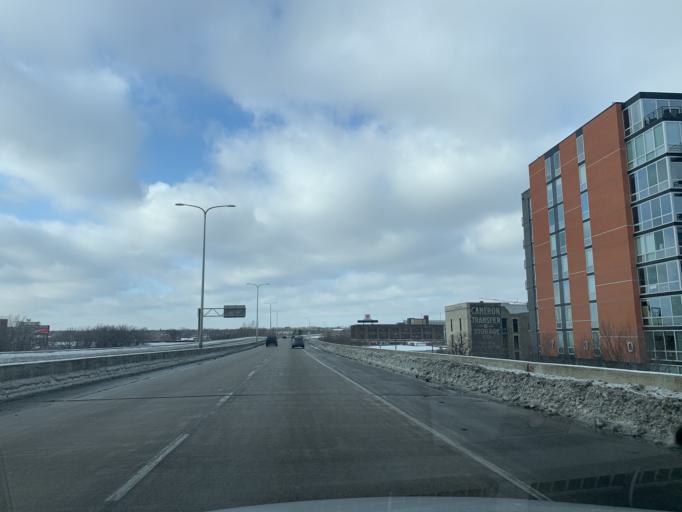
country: US
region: Minnesota
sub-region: Hennepin County
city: Minneapolis
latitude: 44.9862
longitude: -93.2799
